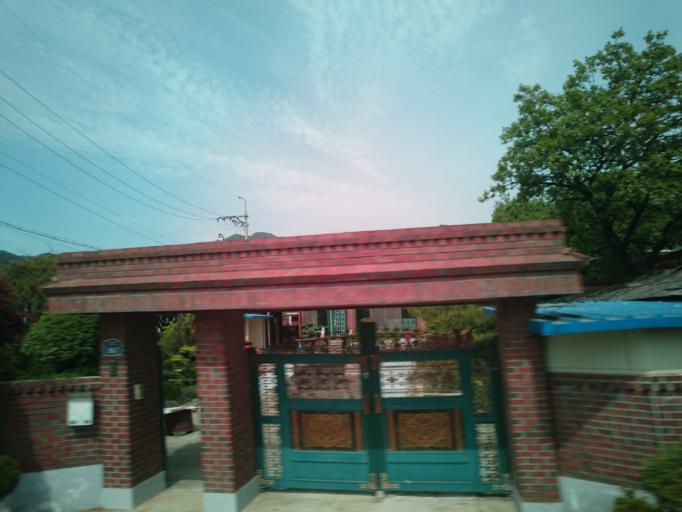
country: KR
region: Jeollabuk-do
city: Wanju
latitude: 35.8960
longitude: 127.1917
